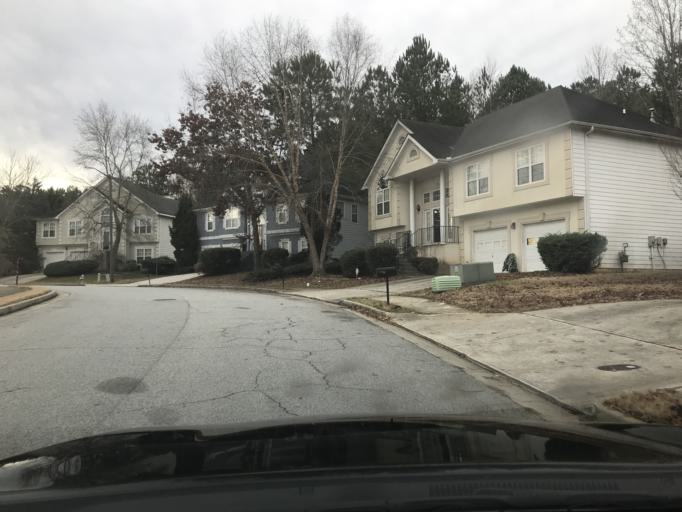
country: US
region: Georgia
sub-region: Fulton County
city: East Point
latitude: 33.7139
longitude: -84.5056
